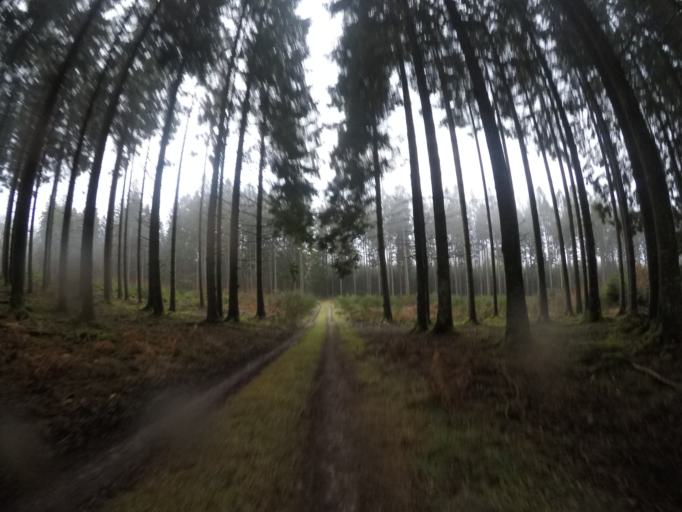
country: BE
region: Wallonia
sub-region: Province du Luxembourg
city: Leglise
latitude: 49.8119
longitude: 5.6045
